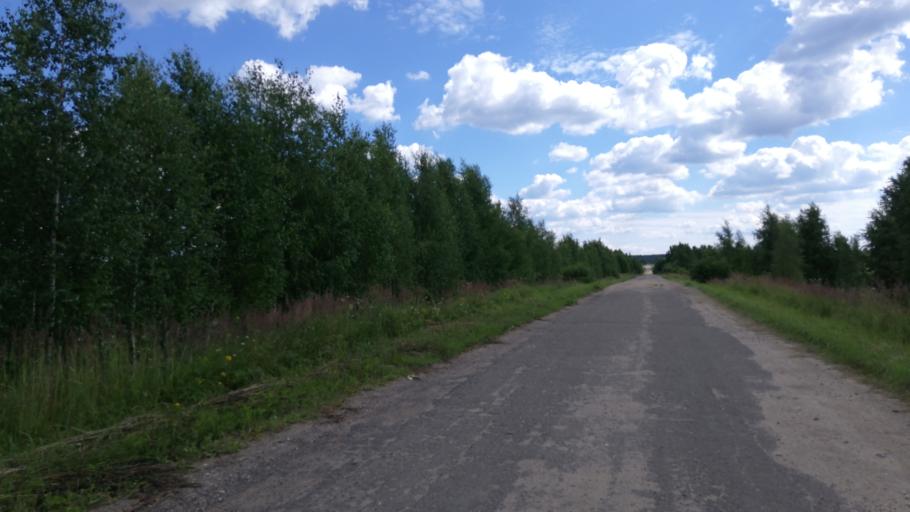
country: RU
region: Jaroslavl
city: Levashevo
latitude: 57.6369
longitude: 40.4636
